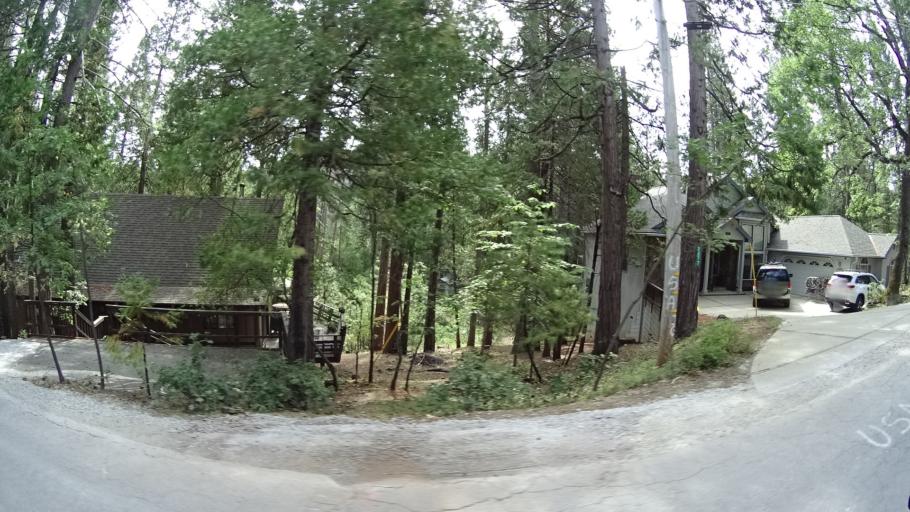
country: US
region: California
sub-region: Calaveras County
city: Arnold
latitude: 38.2469
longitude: -120.3372
